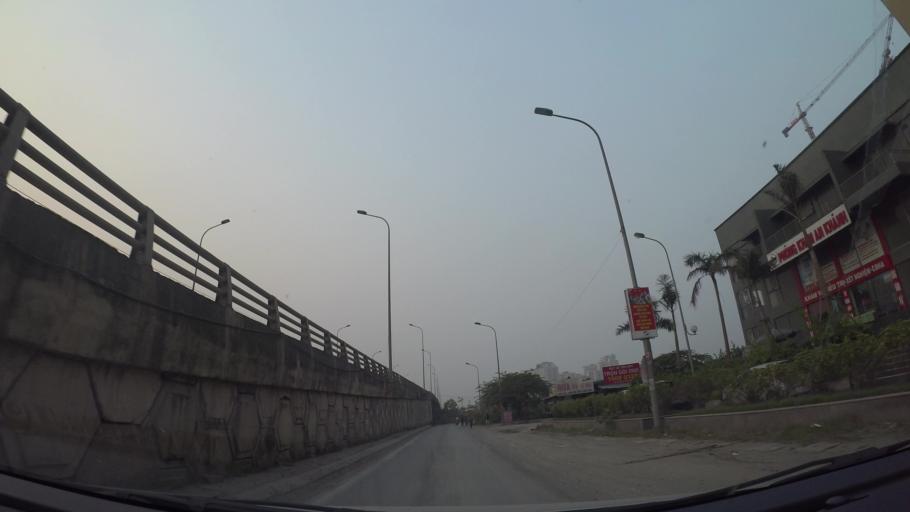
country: VN
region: Ha Noi
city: Cau Dien
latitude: 21.0094
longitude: 105.7206
